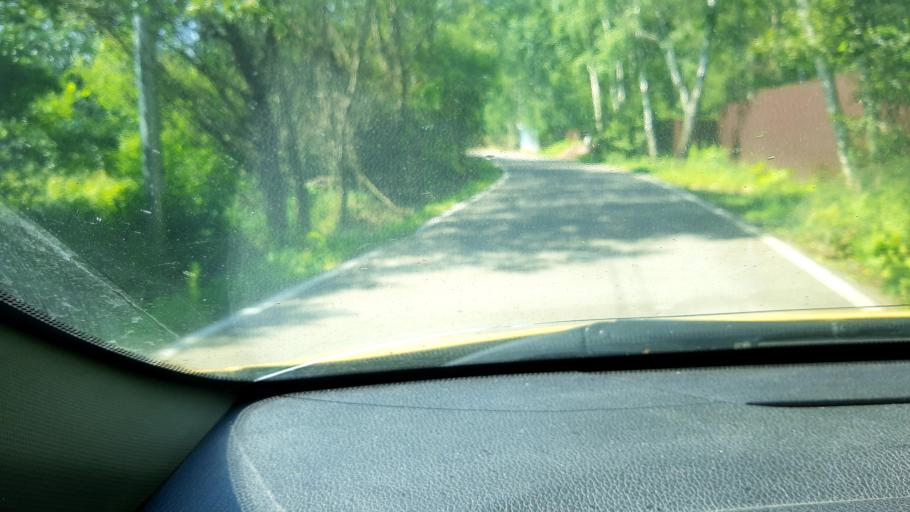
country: RU
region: Moskovskaya
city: Biryulevo Zapadnoye
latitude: 55.5568
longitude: 37.6393
